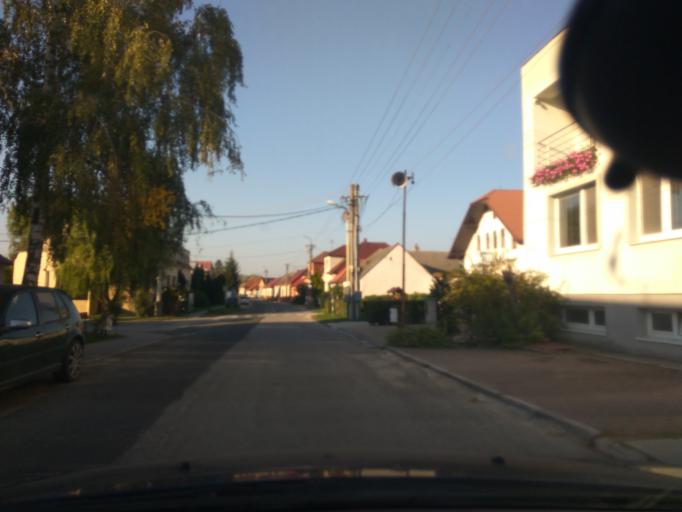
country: SK
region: Trnavsky
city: Vrbove
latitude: 48.5816
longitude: 17.7652
